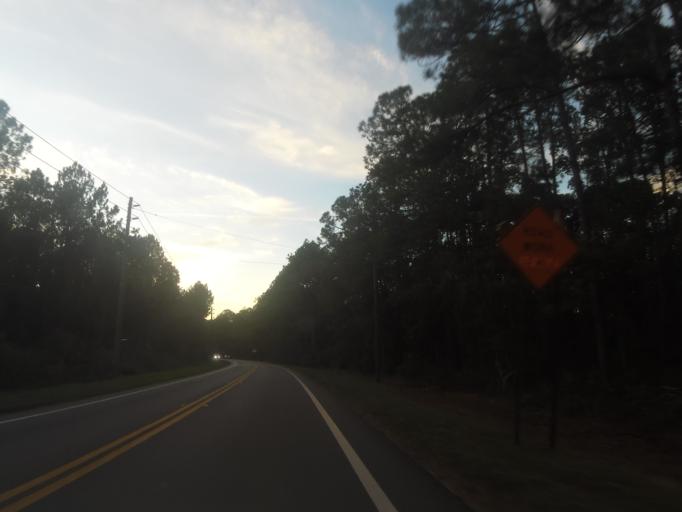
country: US
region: Florida
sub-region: Saint Johns County
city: Fruit Cove
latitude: 30.1037
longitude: -81.5074
